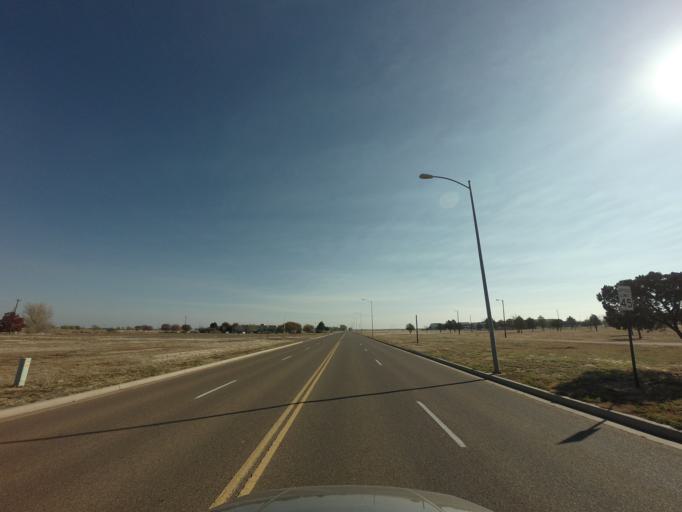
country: US
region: New Mexico
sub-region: Curry County
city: Clovis
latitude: 34.4049
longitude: -103.1674
